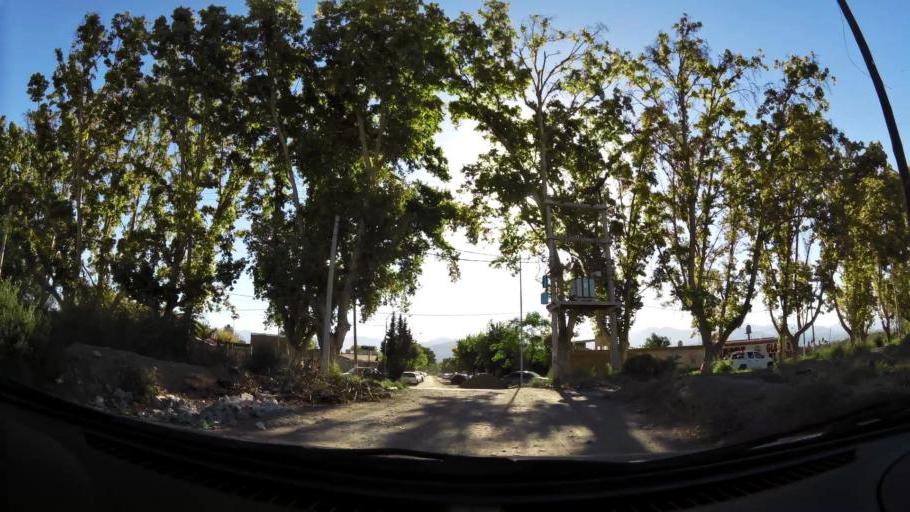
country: AR
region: Mendoza
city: Las Heras
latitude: -32.8476
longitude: -68.8271
